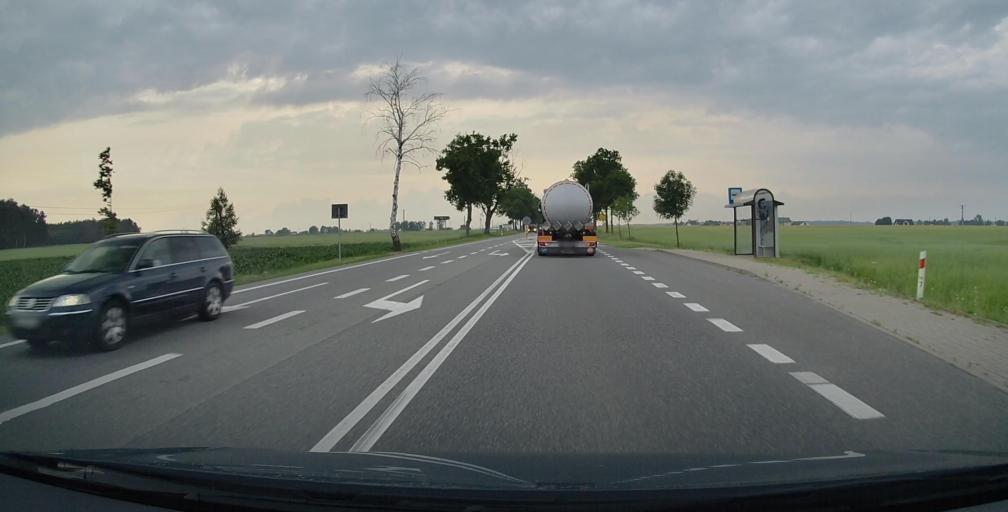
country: PL
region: Masovian Voivodeship
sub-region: Powiat siedlecki
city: Zbuczyn
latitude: 52.1000
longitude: 22.4062
